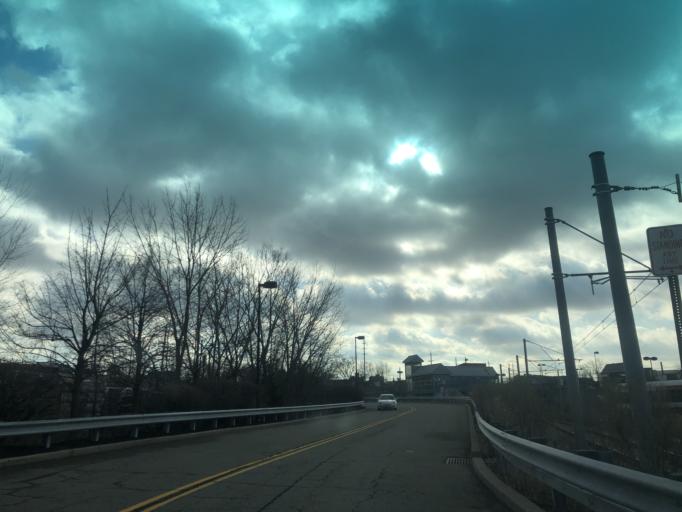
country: US
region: New Jersey
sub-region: Hudson County
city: Union City
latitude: 40.7890
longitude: -74.0318
